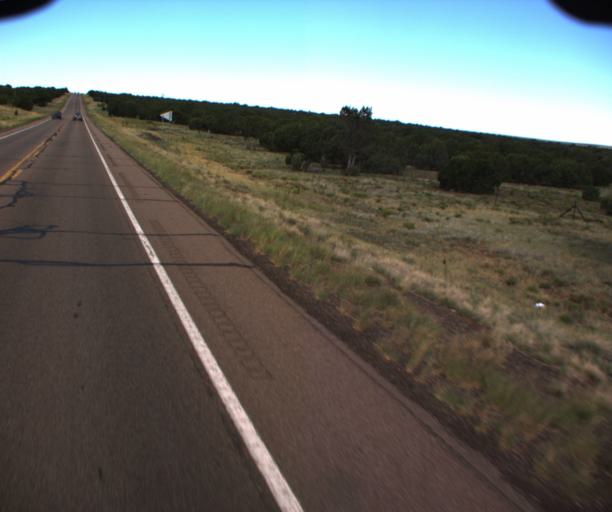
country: US
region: Arizona
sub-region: Navajo County
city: Show Low
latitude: 34.2663
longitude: -109.9496
